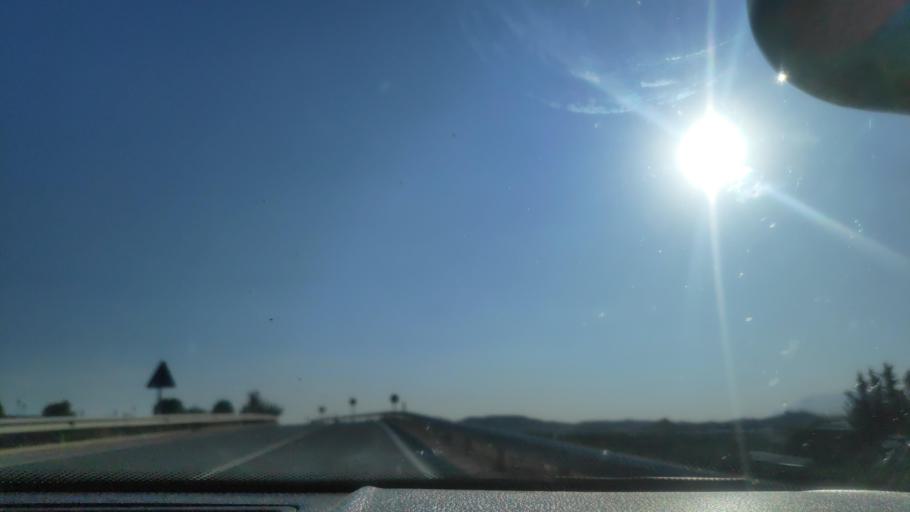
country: ES
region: Andalusia
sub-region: Provincia de Jaen
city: La Guardia de Jaen
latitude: 37.8005
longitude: -3.7186
